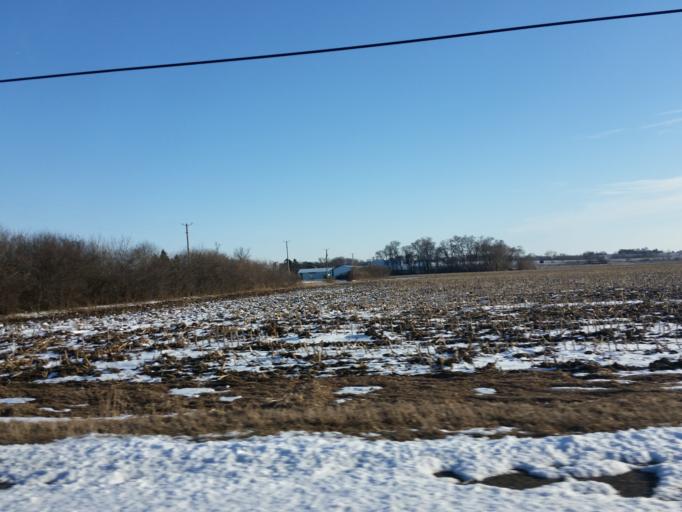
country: US
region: Minnesota
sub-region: Dakota County
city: Rosemount
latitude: 44.7029
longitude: -93.1384
